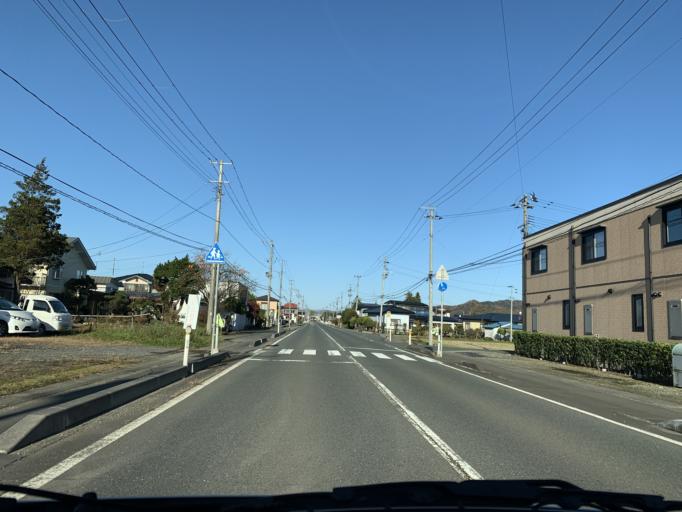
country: JP
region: Iwate
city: Kitakami
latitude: 39.2499
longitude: 141.1060
